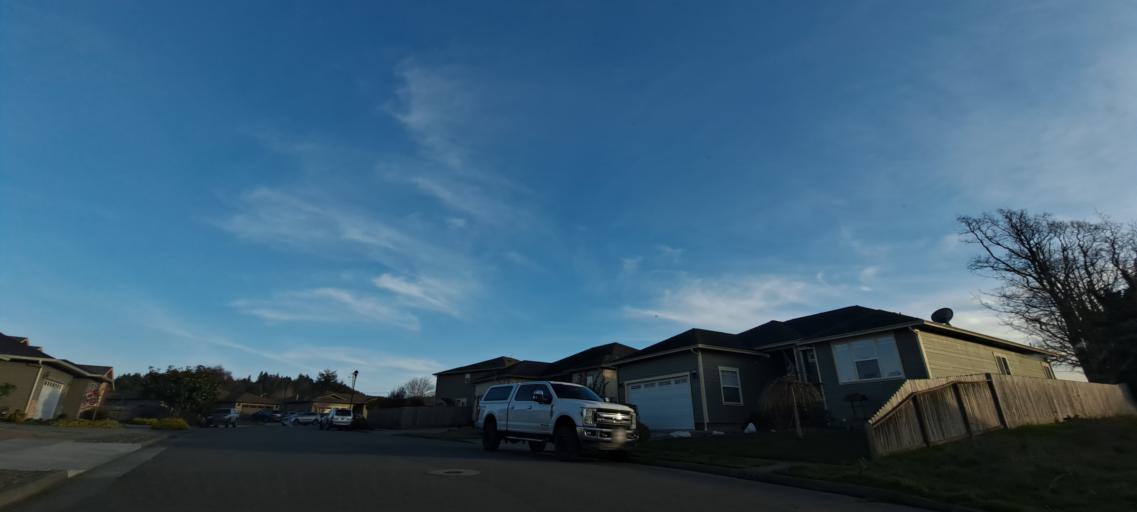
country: US
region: California
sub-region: Humboldt County
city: Fortuna
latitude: 40.5783
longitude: -124.1370
